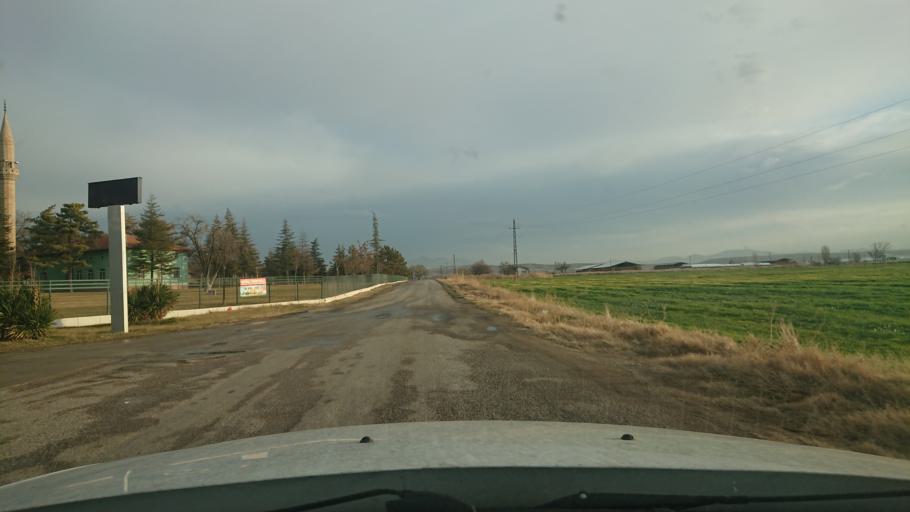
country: TR
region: Aksaray
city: Yesilova
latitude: 38.4569
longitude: 33.8406
